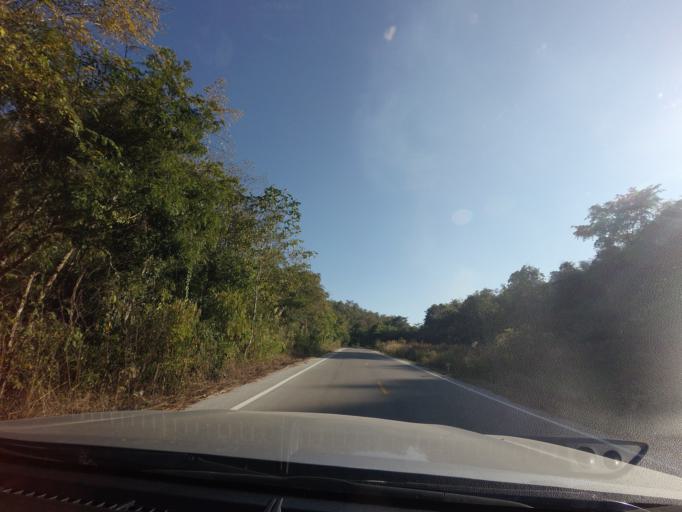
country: TH
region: Lampang
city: Chae Hom
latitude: 18.5822
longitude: 99.6270
